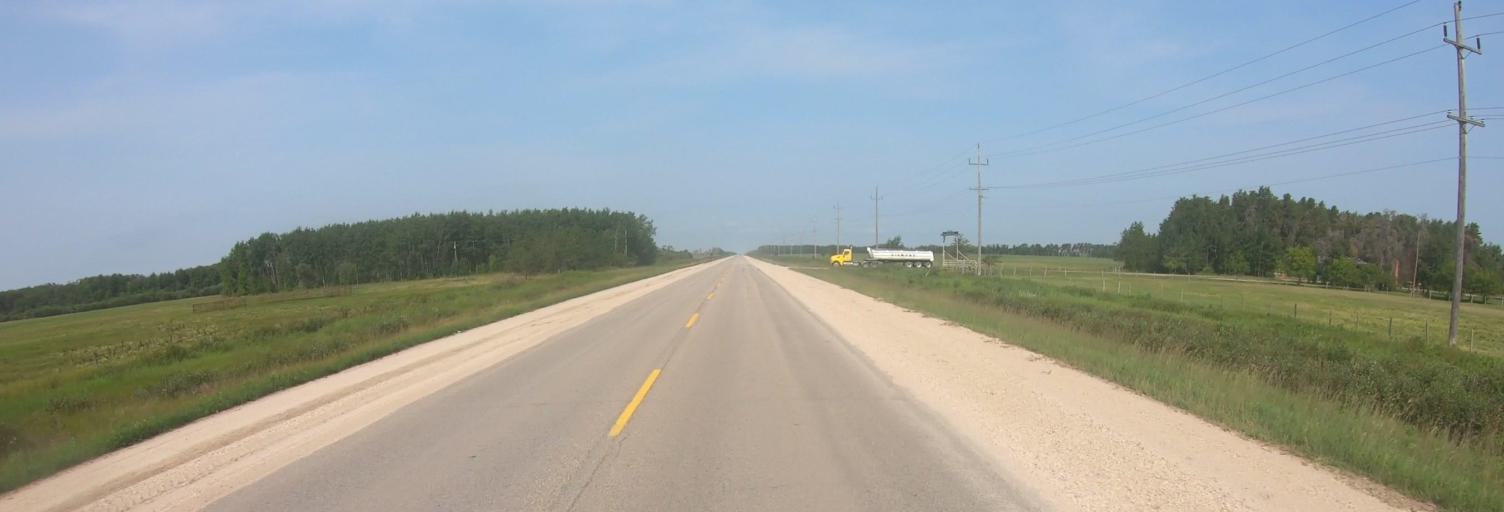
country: CA
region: Manitoba
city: La Broquerie
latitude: 49.3026
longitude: -96.5496
